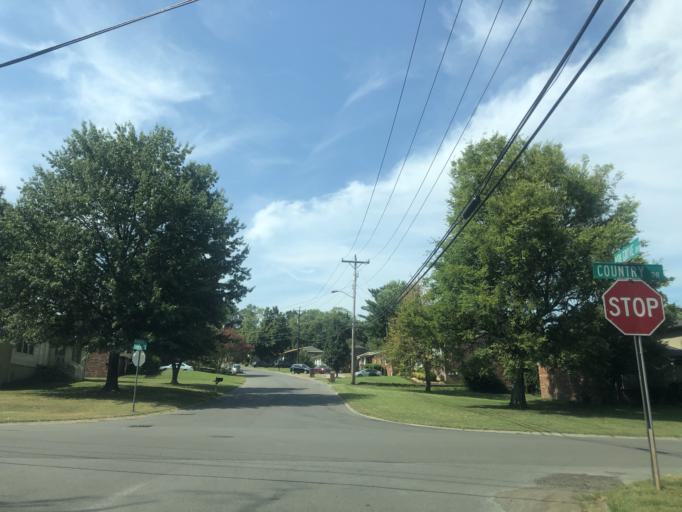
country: US
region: Tennessee
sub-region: Williamson County
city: Brentwood Estates
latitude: 36.0496
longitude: -86.7050
